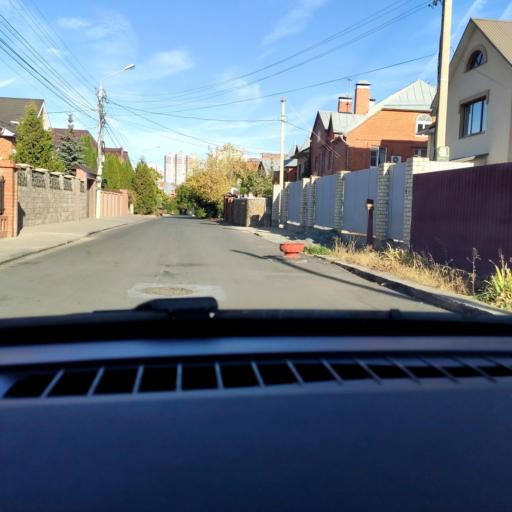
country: RU
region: Voronezj
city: Voronezh
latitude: 51.7058
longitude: 39.2036
